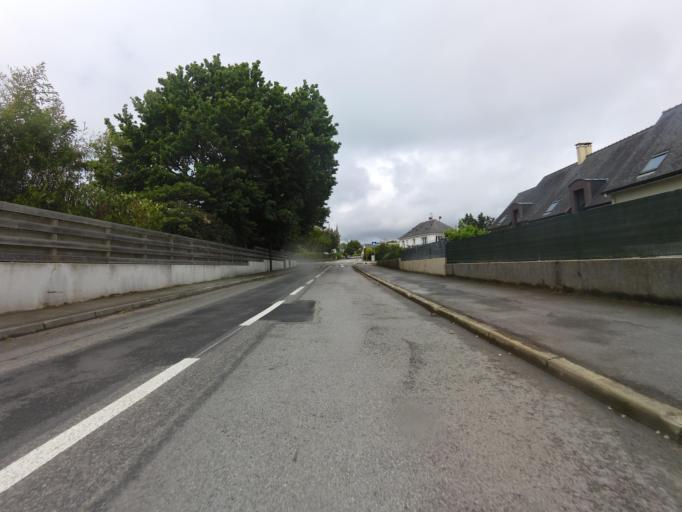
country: FR
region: Brittany
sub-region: Departement du Morbihan
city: Baden
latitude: 47.6161
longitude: -2.9209
